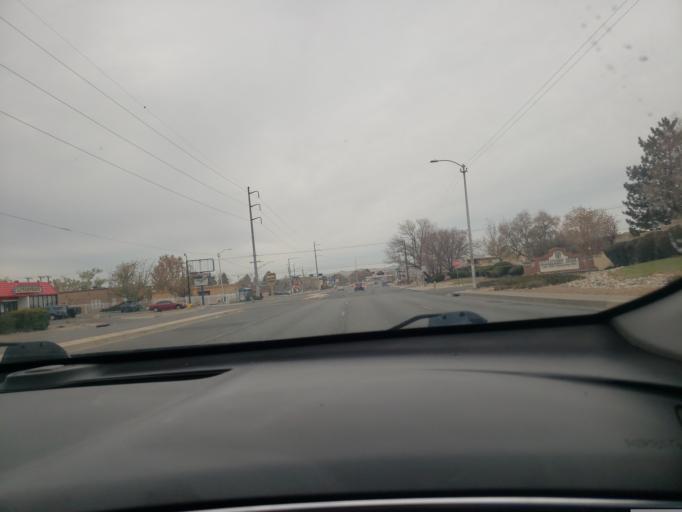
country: US
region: New Mexico
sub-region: Bernalillo County
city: North Valley
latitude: 35.1310
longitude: -106.6019
